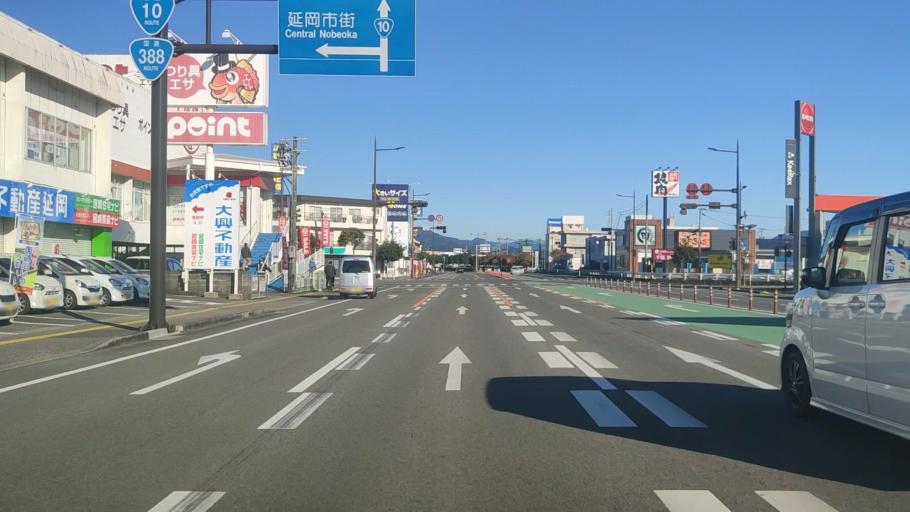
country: JP
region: Miyazaki
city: Nobeoka
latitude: 32.5752
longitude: 131.6835
